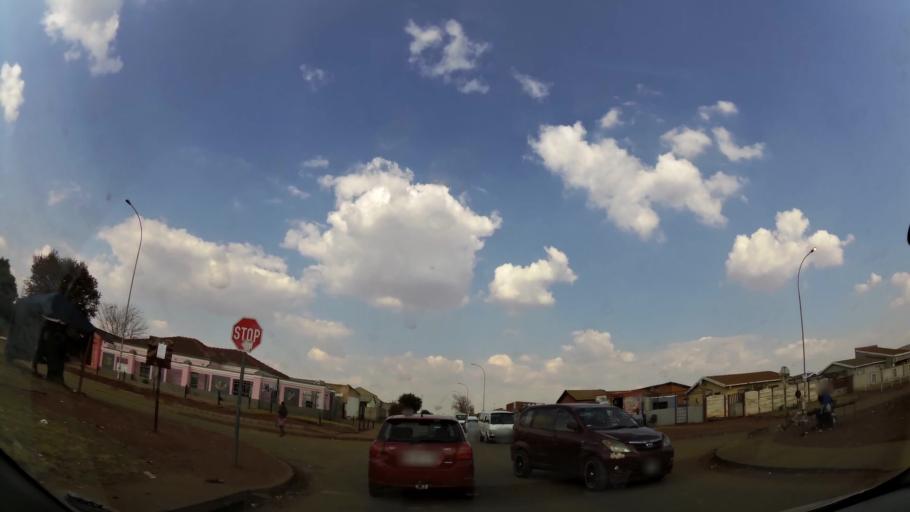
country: ZA
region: Gauteng
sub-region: Ekurhuleni Metropolitan Municipality
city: Germiston
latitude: -26.3178
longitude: 28.2006
